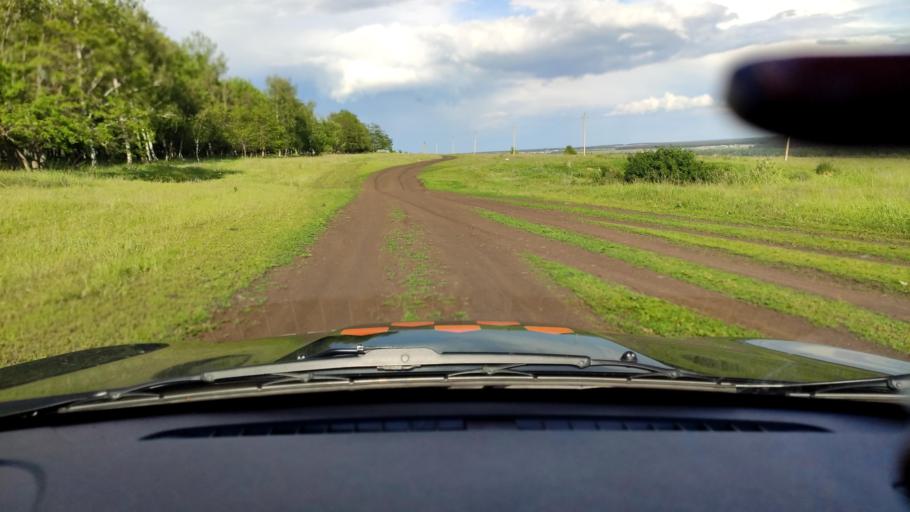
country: RU
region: Voronezj
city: Uryv-Pokrovka
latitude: 51.1198
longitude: 39.1974
